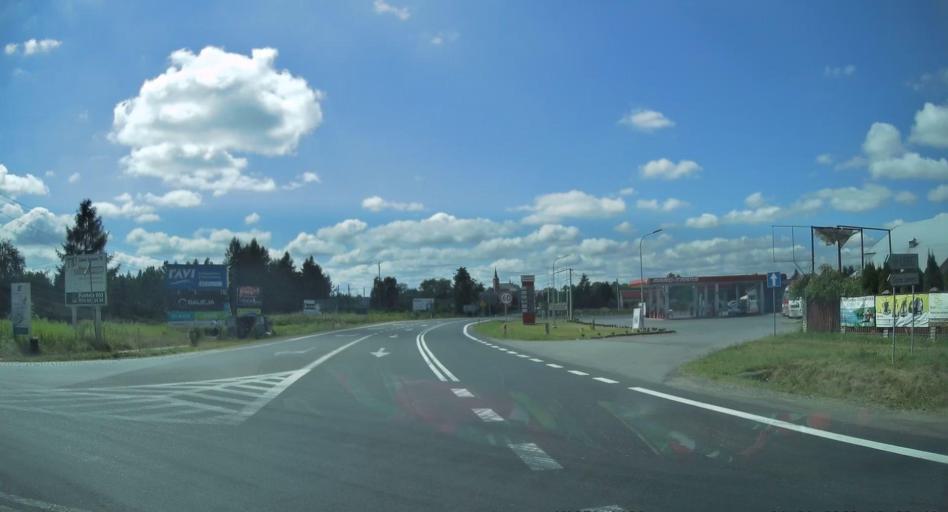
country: PL
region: Subcarpathian Voivodeship
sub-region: Powiat debicki
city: Brzeznica
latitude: 50.1095
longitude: 21.4896
